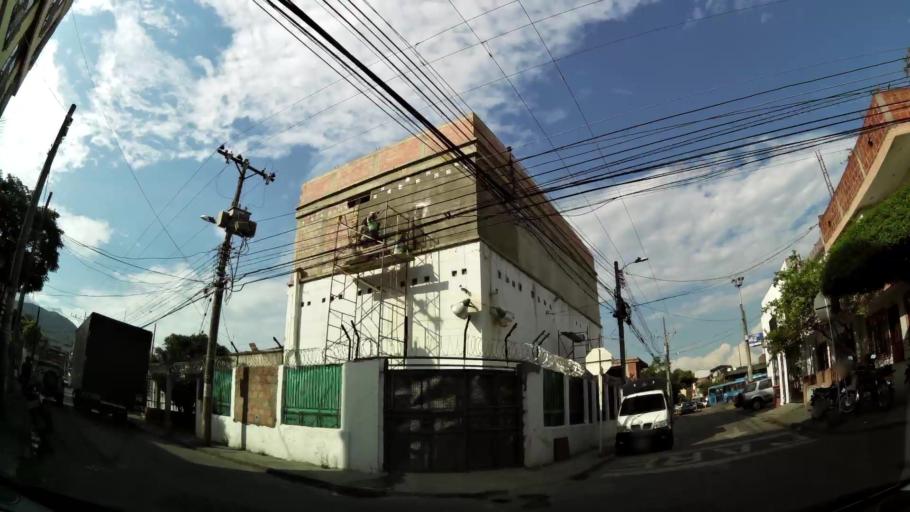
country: CO
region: Valle del Cauca
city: Cali
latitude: 3.4702
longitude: -76.5111
